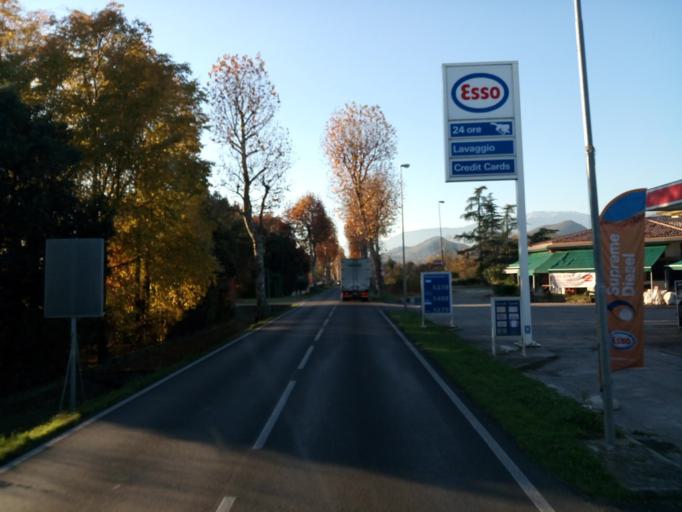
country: IT
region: Veneto
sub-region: Provincia di Treviso
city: Maser
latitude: 45.7929
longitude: 11.9726
